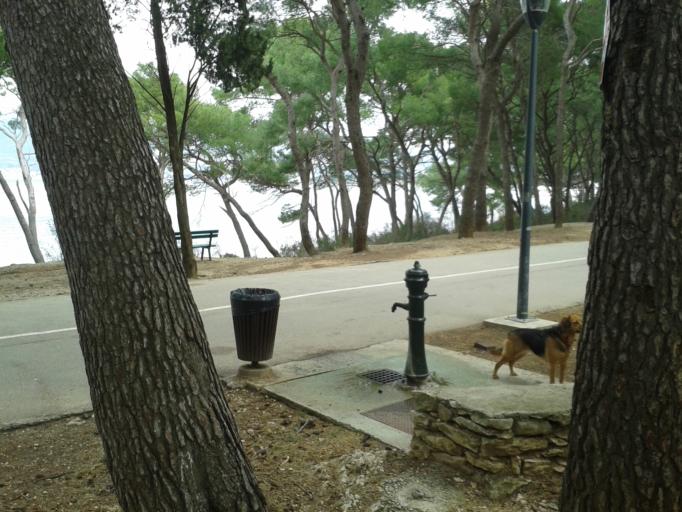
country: HR
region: Splitsko-Dalmatinska
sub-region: Grad Split
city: Split
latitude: 43.5143
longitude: 16.4096
